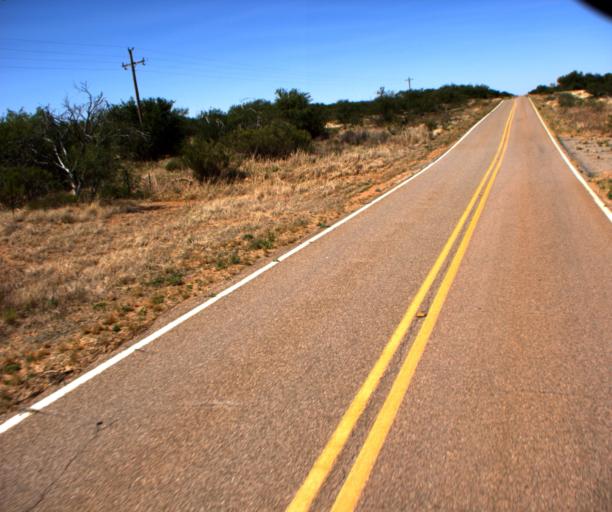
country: US
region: Arizona
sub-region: Pima County
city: Arivaca Junction
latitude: 31.6265
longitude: -111.5102
